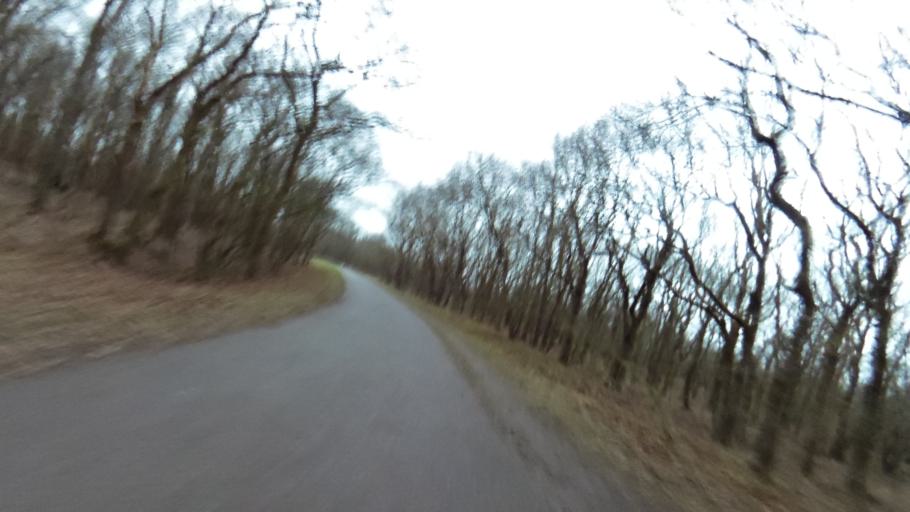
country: NL
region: North Holland
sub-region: Gemeente Castricum
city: Castricum
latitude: 52.5432
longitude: 4.6252
